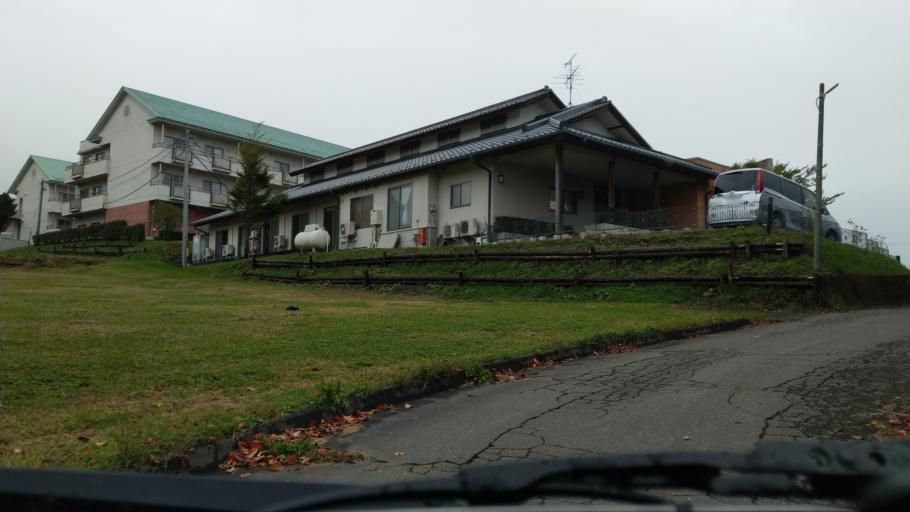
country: JP
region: Nagano
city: Komoro
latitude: 36.3371
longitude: 138.4533
